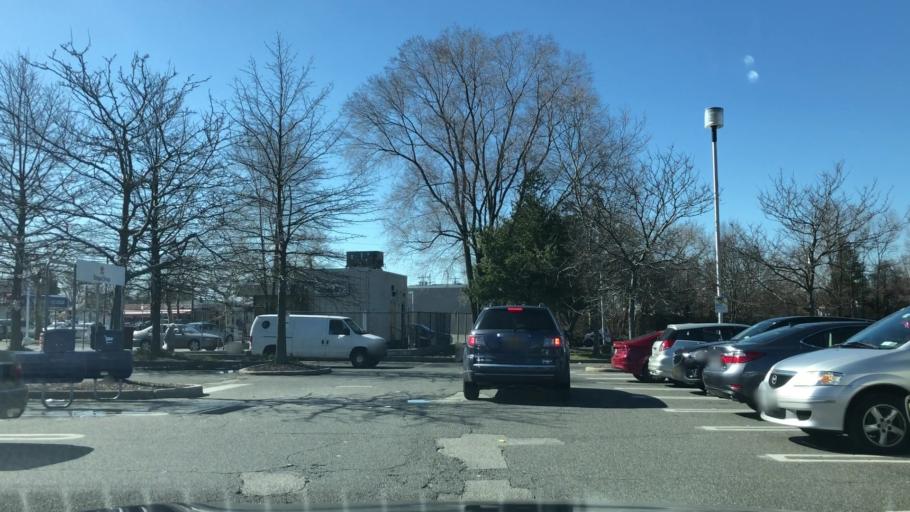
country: US
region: New York
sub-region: Nassau County
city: Franklin Square
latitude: 40.6945
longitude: -73.6835
